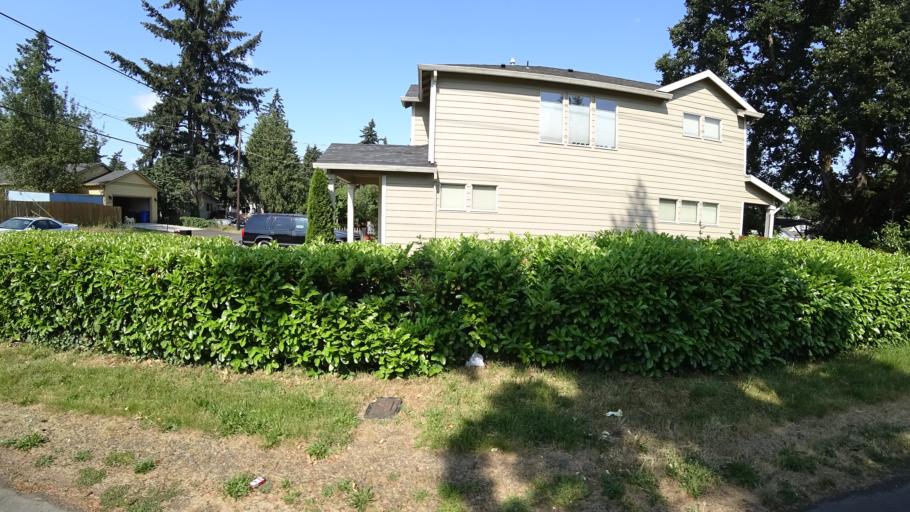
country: US
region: Oregon
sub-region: Multnomah County
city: Lents
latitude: 45.4544
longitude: -122.5959
